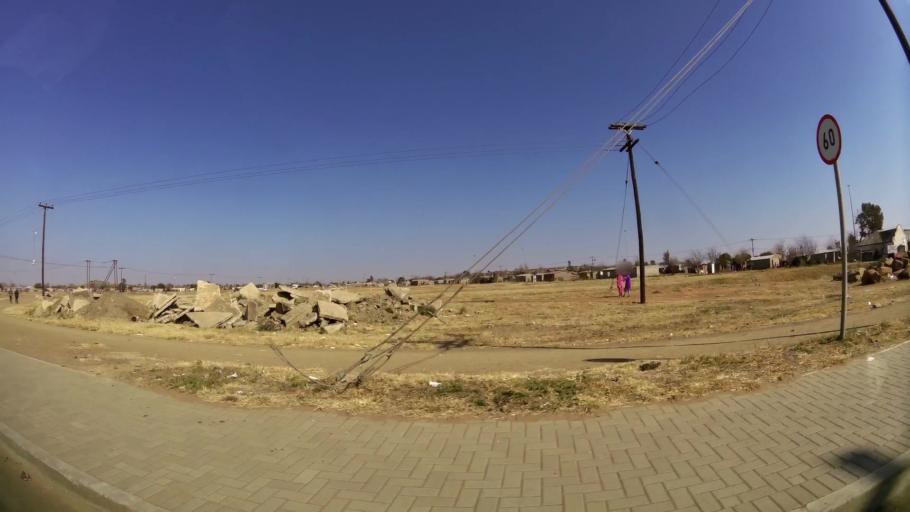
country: ZA
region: Orange Free State
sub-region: Mangaung Metropolitan Municipality
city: Bloemfontein
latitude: -29.1606
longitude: 26.2561
